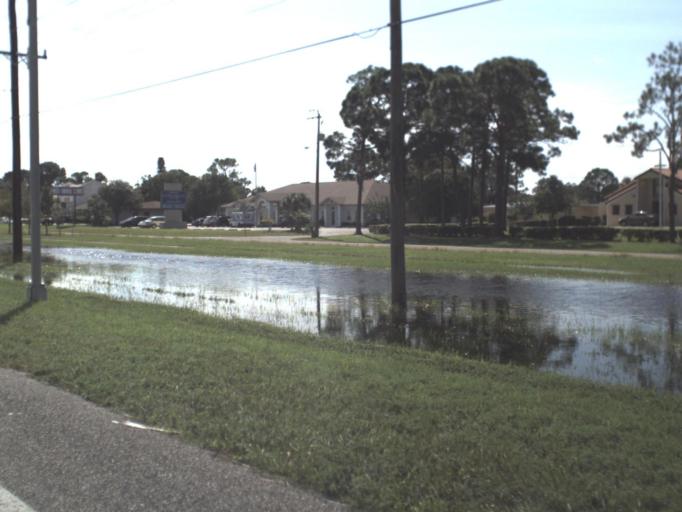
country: US
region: Florida
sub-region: Sarasota County
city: North Port
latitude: 27.0431
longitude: -82.2347
